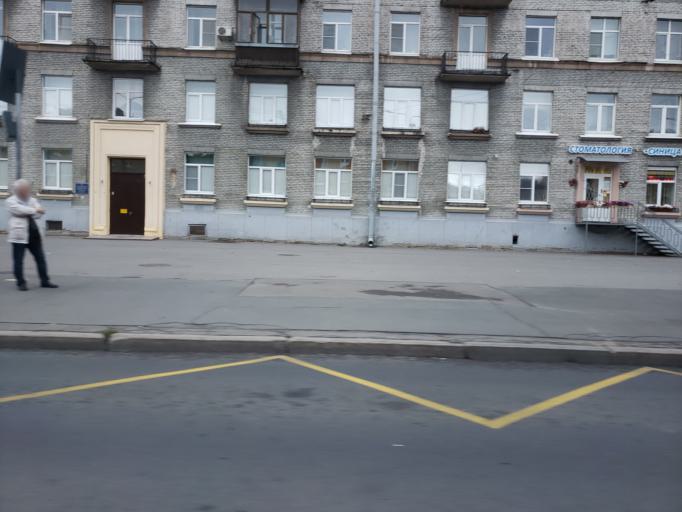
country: RU
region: St.-Petersburg
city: Vasyl'evsky Ostrov
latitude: 59.9371
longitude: 30.2335
